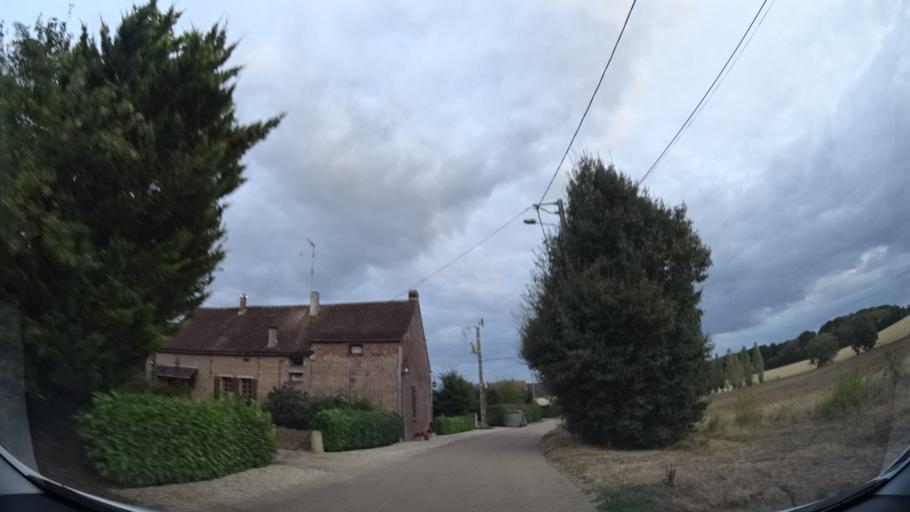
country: FR
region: Bourgogne
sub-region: Departement de l'Yonne
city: Cezy
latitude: 47.9367
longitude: 3.2765
